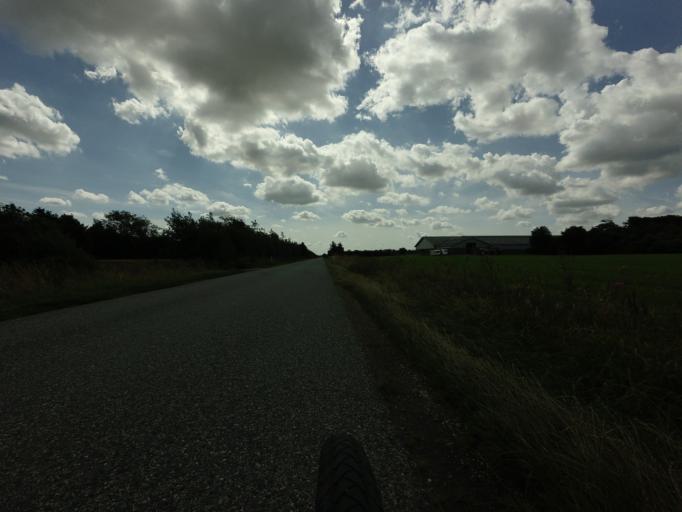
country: DK
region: North Denmark
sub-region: Hjorring Kommune
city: Hjorring
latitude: 57.4609
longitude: 9.9057
